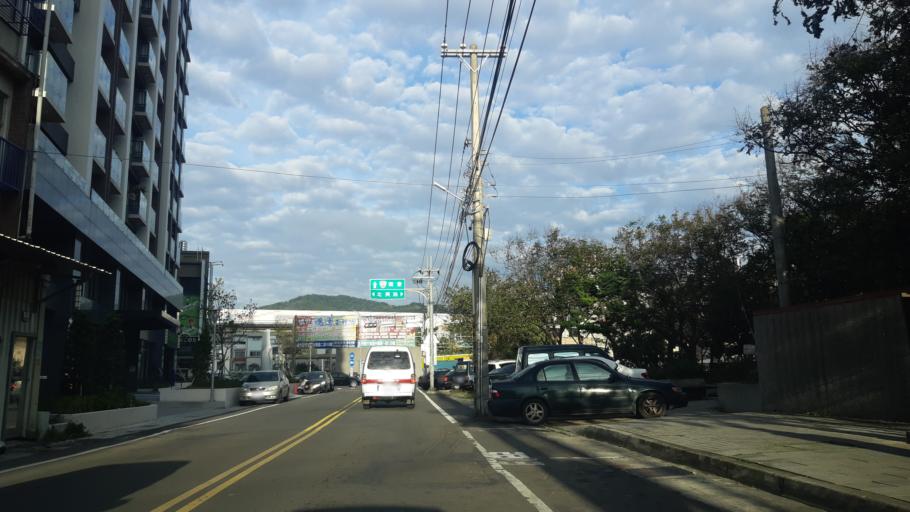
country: TW
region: Taiwan
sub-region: Hsinchu
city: Zhubei
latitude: 24.7417
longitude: 121.0894
